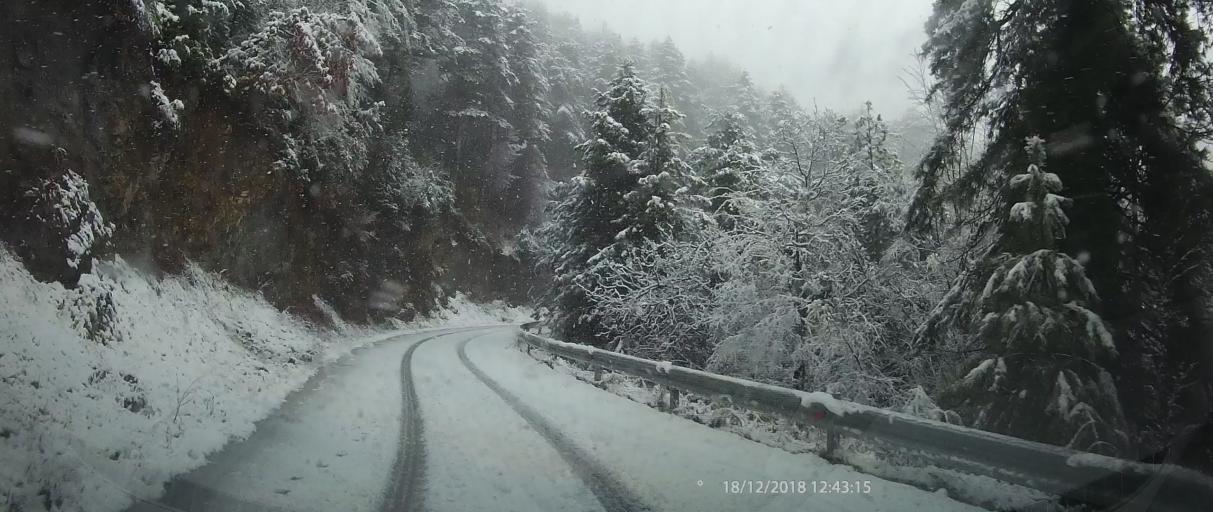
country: GR
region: Central Macedonia
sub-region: Nomos Pierias
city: Litochoro
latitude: 40.0965
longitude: 22.4226
